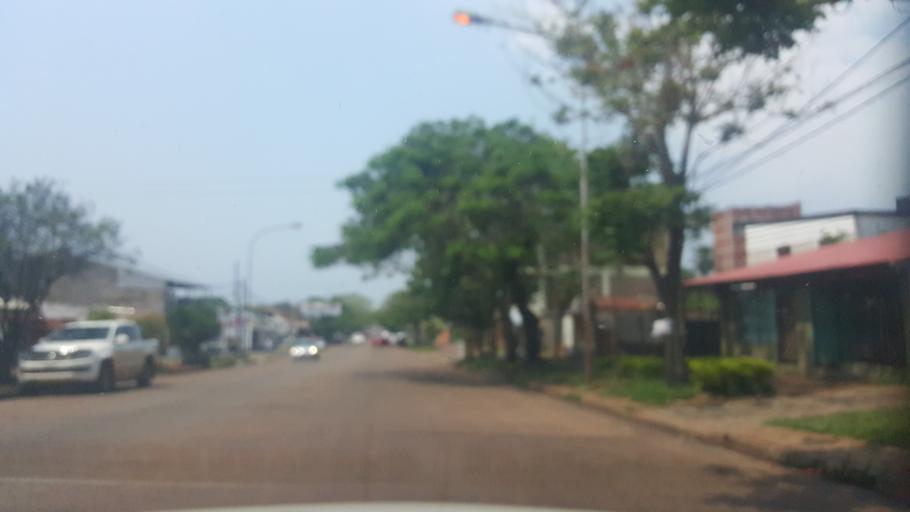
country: AR
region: Misiones
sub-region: Departamento de Capital
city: Posadas
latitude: -27.3870
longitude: -55.9060
